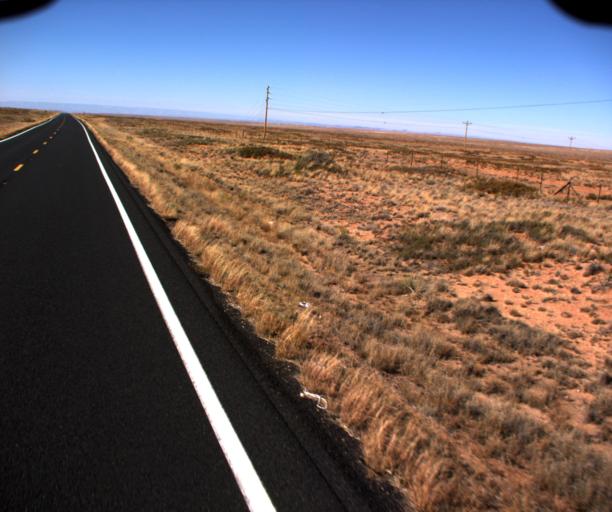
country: US
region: Arizona
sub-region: Coconino County
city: Tuba City
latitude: 36.0099
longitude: -111.0652
